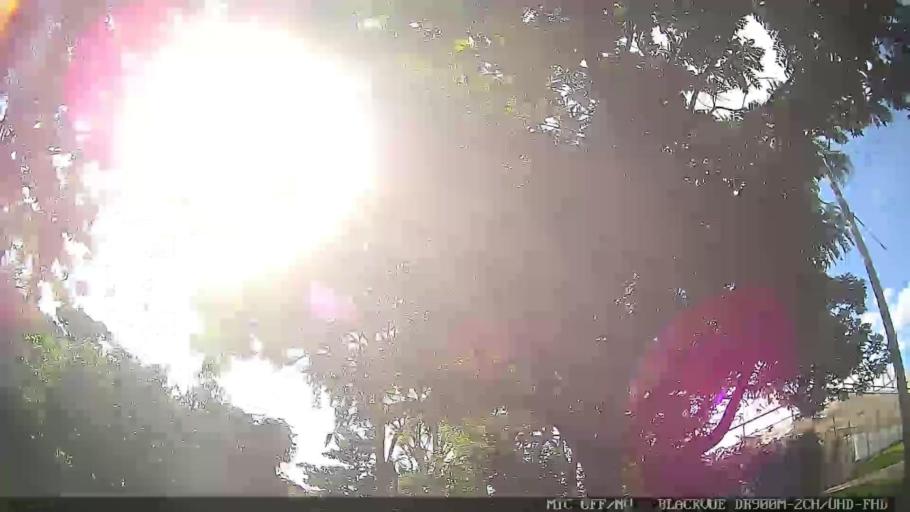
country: BR
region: Sao Paulo
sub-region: Artur Nogueira
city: Artur Nogueira
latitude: -22.6373
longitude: -47.0870
